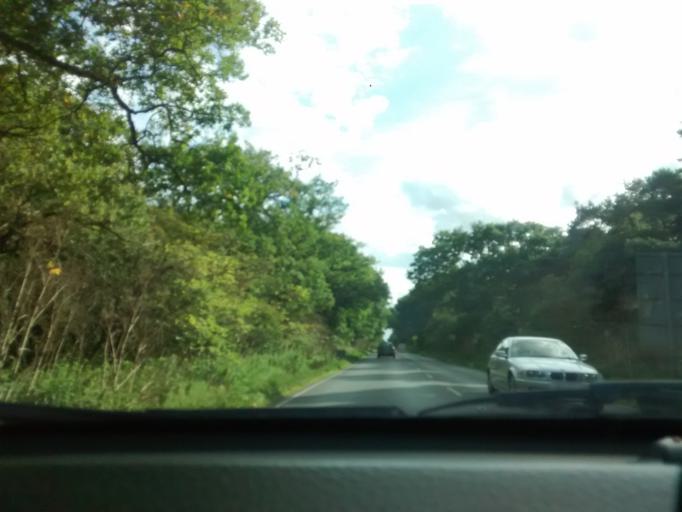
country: GB
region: England
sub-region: Norfolk
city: King's Lynn
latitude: 52.6807
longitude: 0.4211
